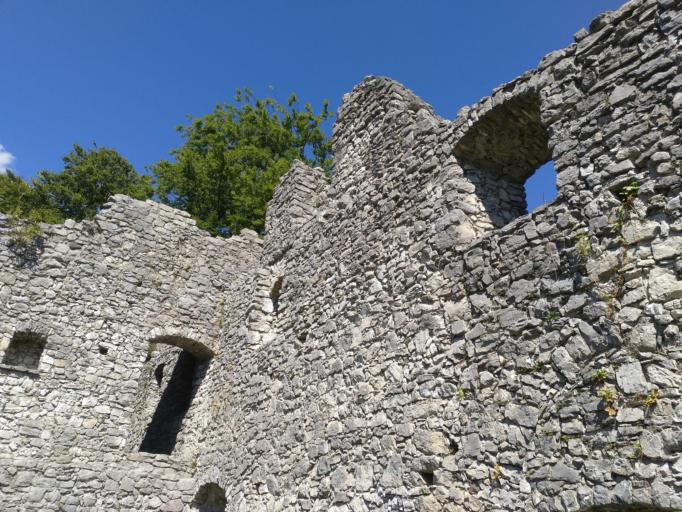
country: DE
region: Bavaria
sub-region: Upper Bavaria
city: Farchant
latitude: 47.5163
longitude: 11.0920
